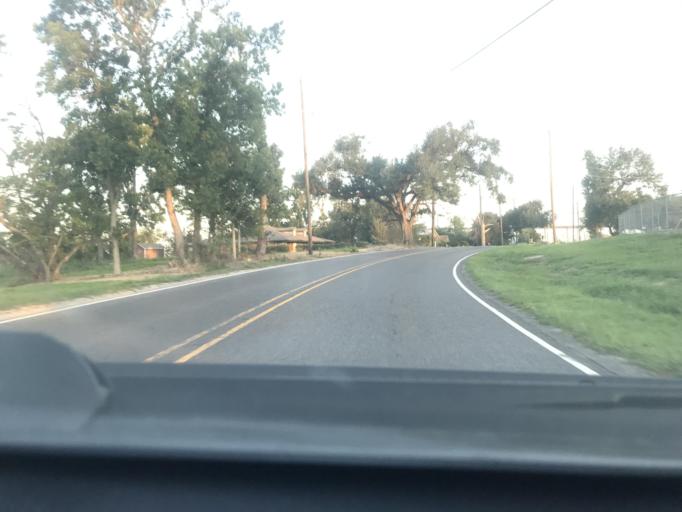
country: US
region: Louisiana
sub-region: Calcasieu Parish
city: Westlake
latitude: 30.2443
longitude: -93.2507
